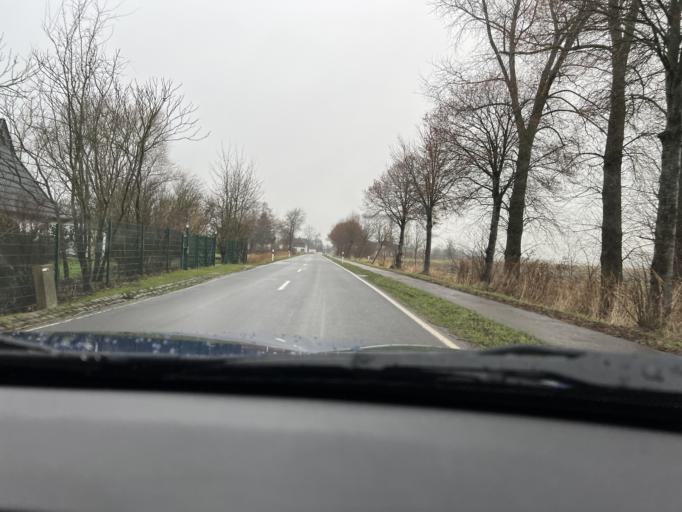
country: DE
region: Schleswig-Holstein
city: Stelle-Wittenwurth
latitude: 54.2335
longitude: 9.0485
